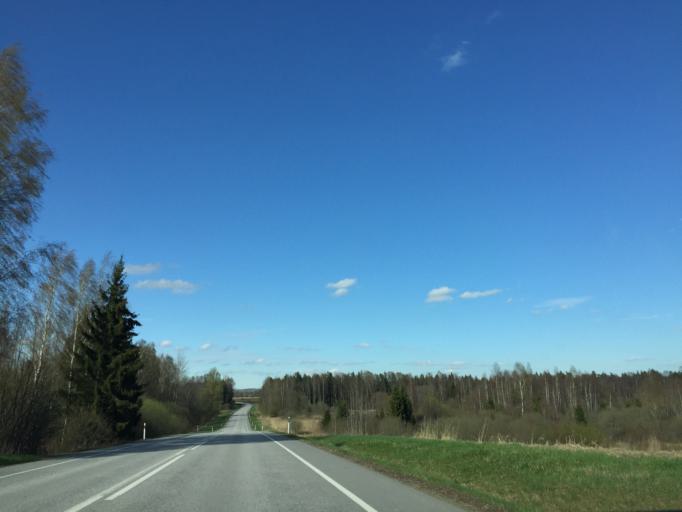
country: EE
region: Vorumaa
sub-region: Antsla vald
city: Vana-Antsla
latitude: 57.8854
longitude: 26.2844
